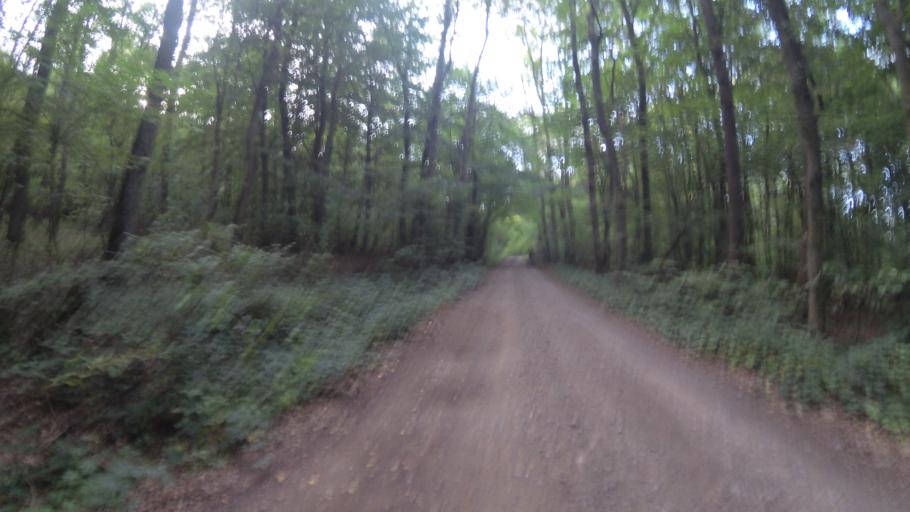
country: DE
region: Saarland
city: Namborn
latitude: 49.5386
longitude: 7.1336
